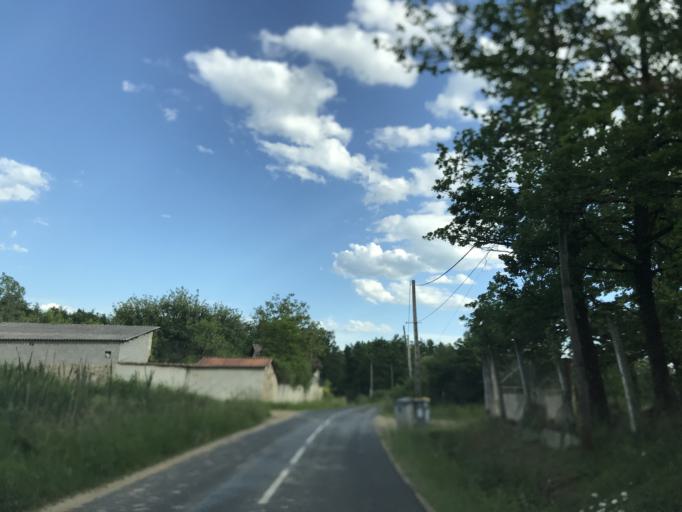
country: FR
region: Auvergne
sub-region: Departement du Puy-de-Dome
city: Courpiere
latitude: 45.7652
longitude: 3.6010
